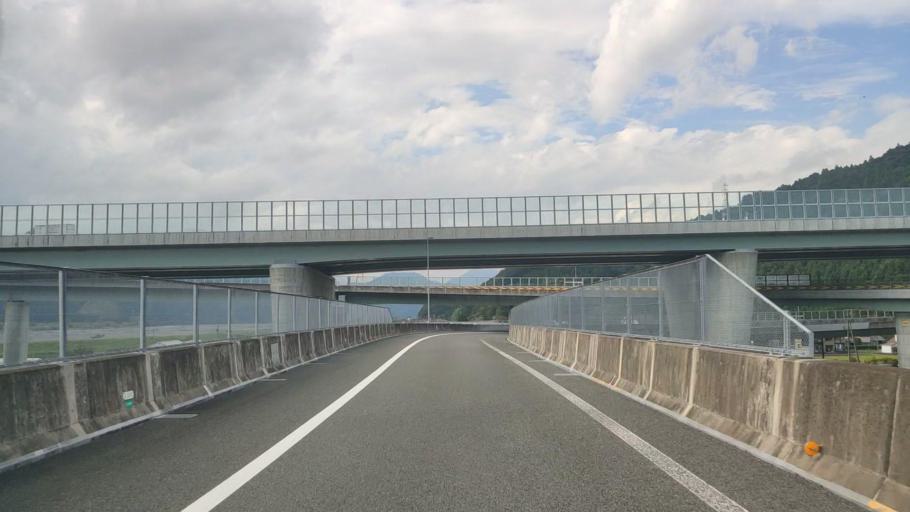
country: JP
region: Shizuoka
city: Shizuoka-shi
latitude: 35.0404
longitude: 138.3779
